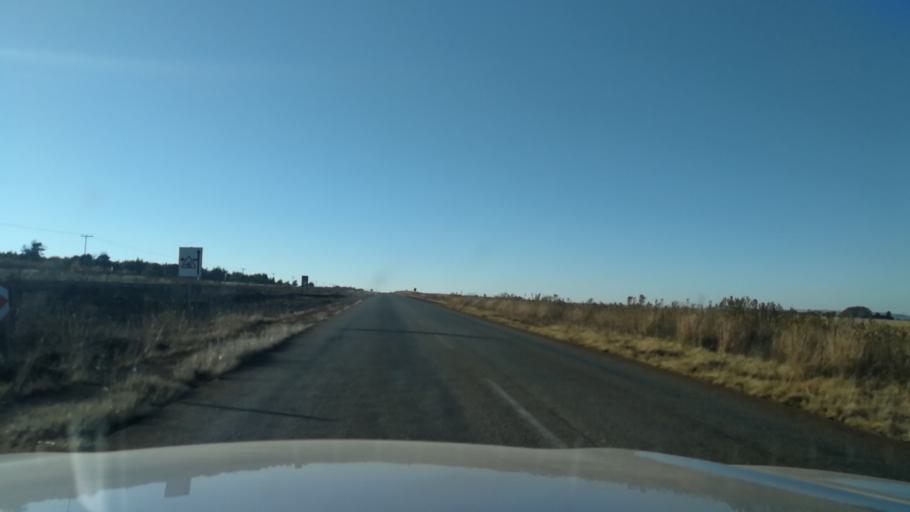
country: ZA
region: North-West
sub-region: Bojanala Platinum District Municipality
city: Koster
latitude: -25.9354
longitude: 27.1454
